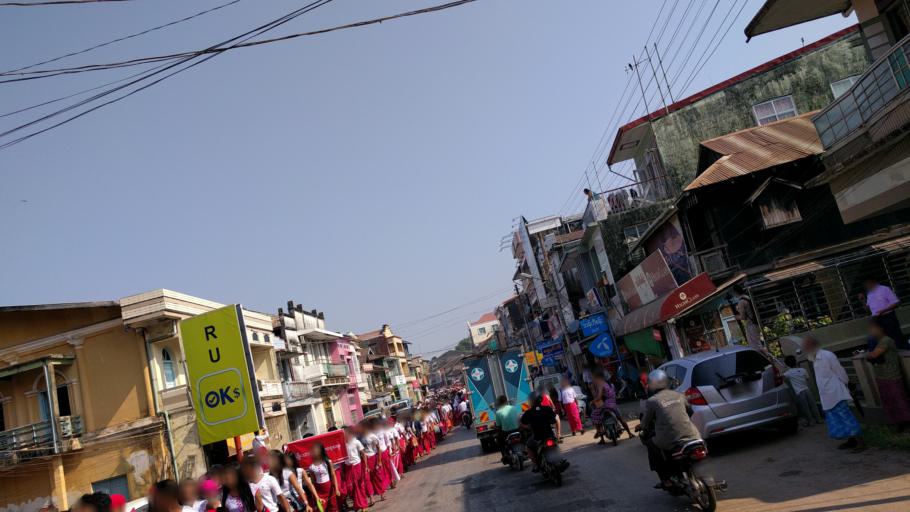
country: MM
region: Mon
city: Mawlamyine
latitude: 16.4864
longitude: 97.6191
